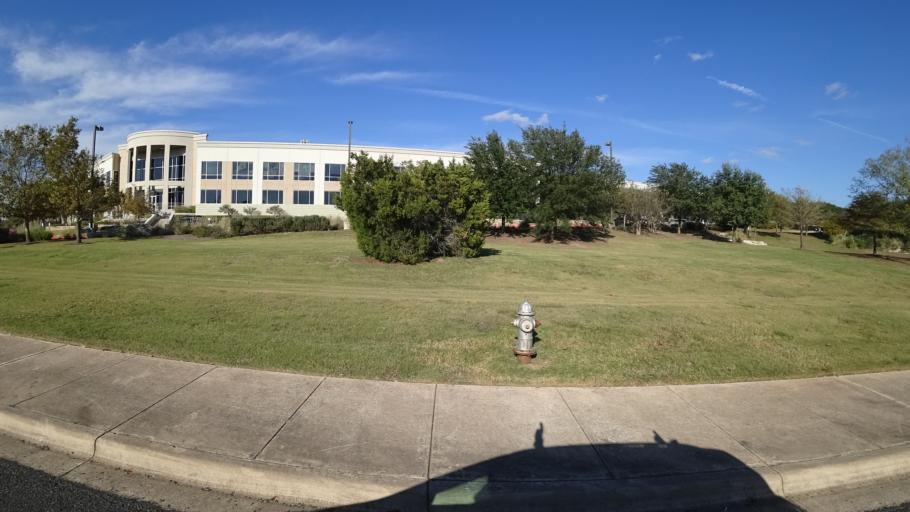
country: US
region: Texas
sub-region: Travis County
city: Barton Creek
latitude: 30.2531
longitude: -97.8723
